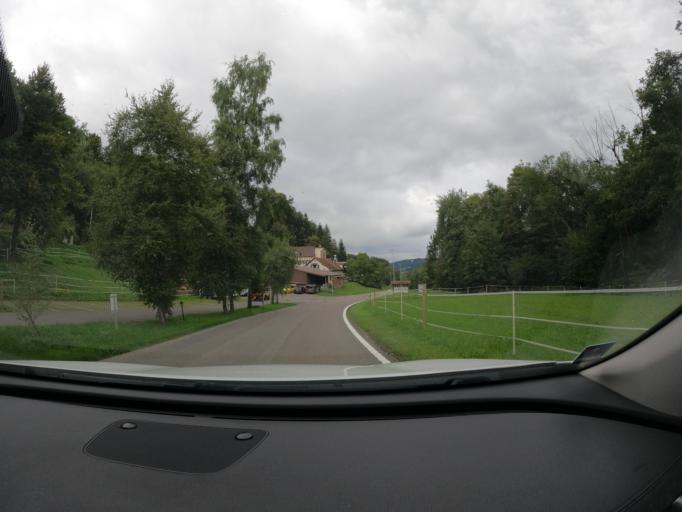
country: CH
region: Aargau
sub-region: Bezirk Kulm
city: Gontenschwil
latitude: 47.2578
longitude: 8.1383
